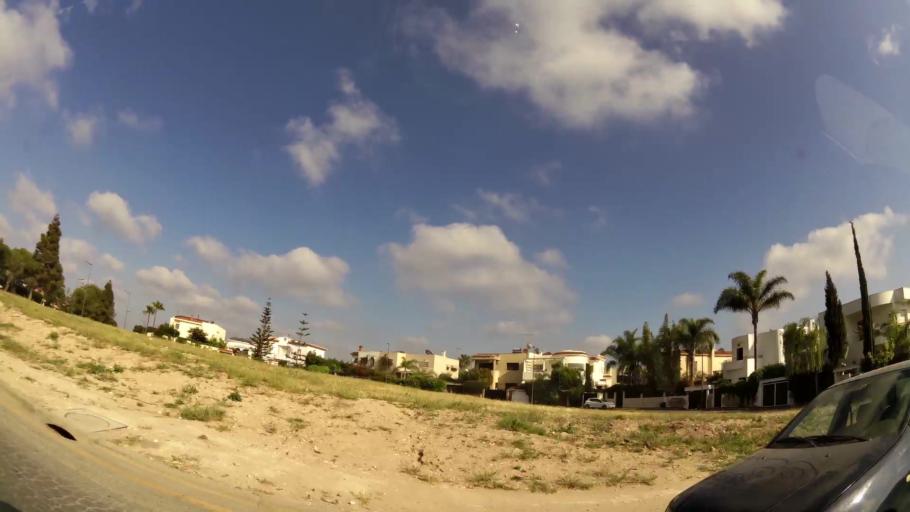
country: MA
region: Rabat-Sale-Zemmour-Zaer
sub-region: Skhirate-Temara
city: Temara
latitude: 33.9497
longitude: -6.8685
